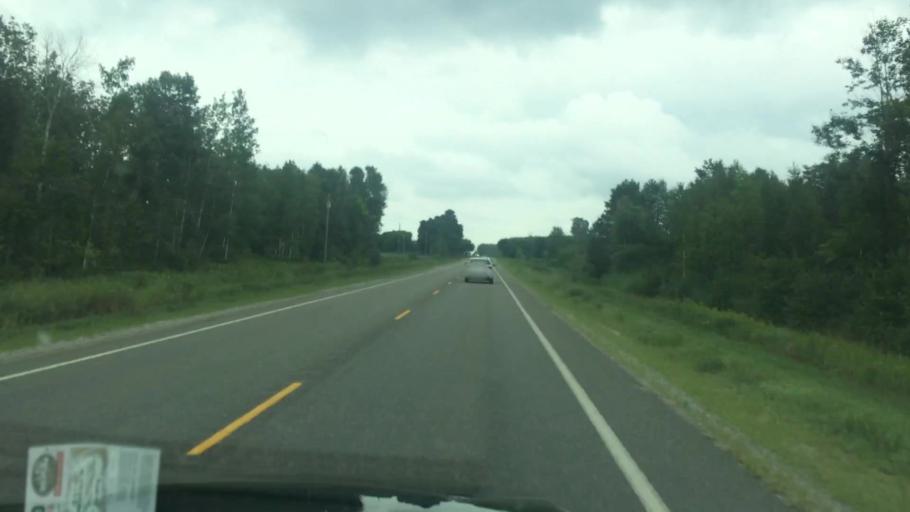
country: US
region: Michigan
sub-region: Tuscola County
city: Cass City
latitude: 43.6280
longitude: -83.0971
